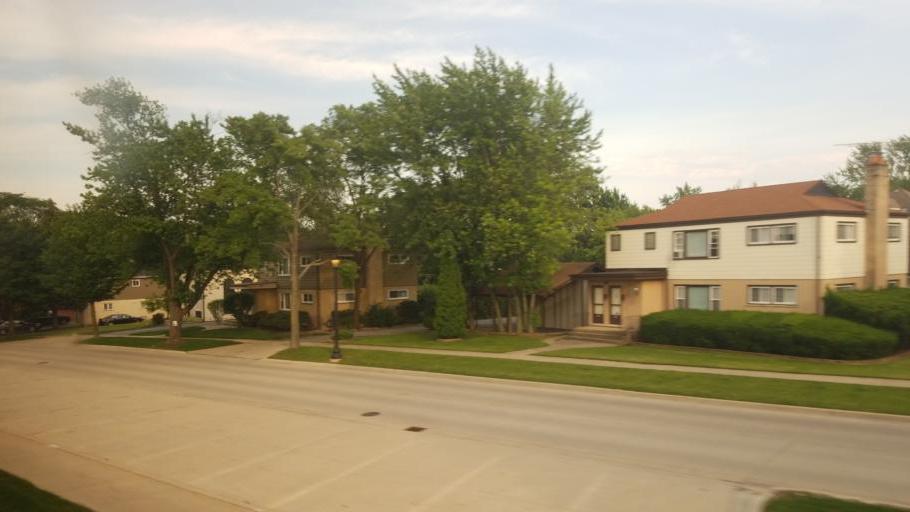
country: US
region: Illinois
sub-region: Cook County
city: Western Springs
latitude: 41.8106
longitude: -87.8945
